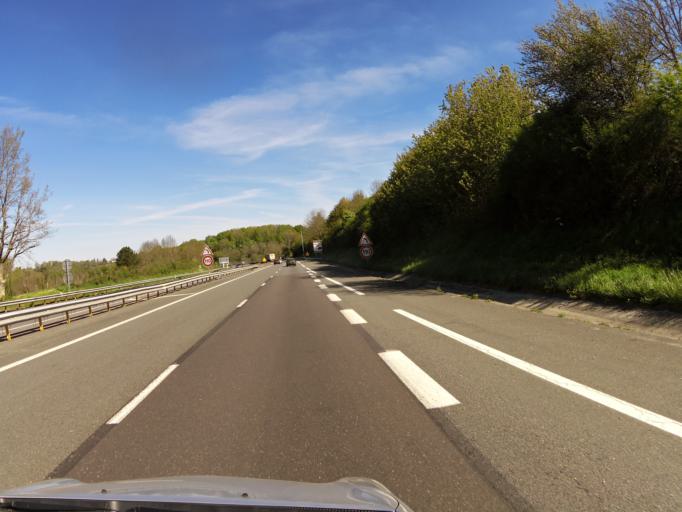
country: FR
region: Limousin
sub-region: Departement de la Haute-Vienne
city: Pierre-Buffiere
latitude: 45.6922
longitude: 1.3663
